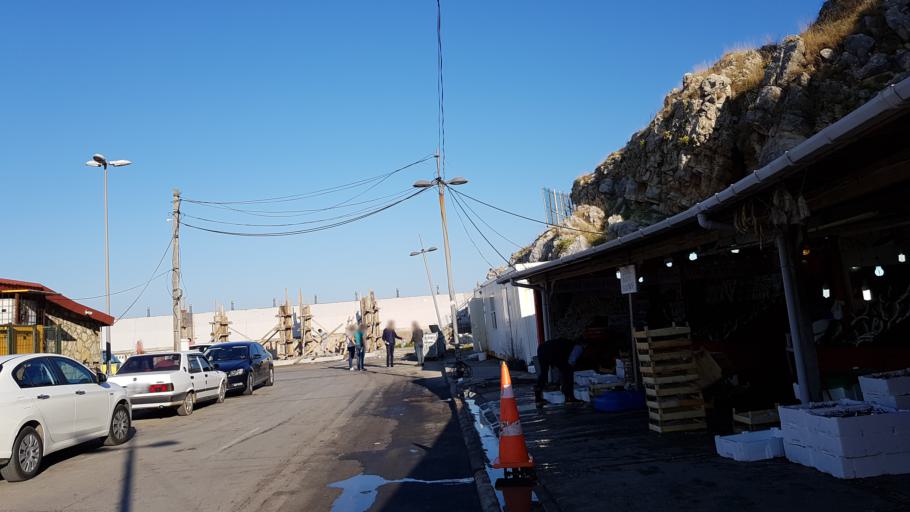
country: TR
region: Istanbul
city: Sile
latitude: 41.1813
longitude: 29.6070
